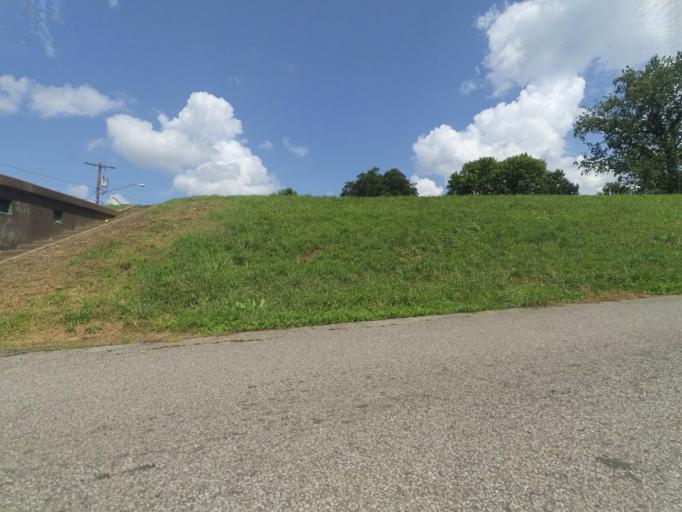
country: US
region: West Virginia
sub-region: Cabell County
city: Pea Ridge
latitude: 38.4161
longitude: -82.3600
